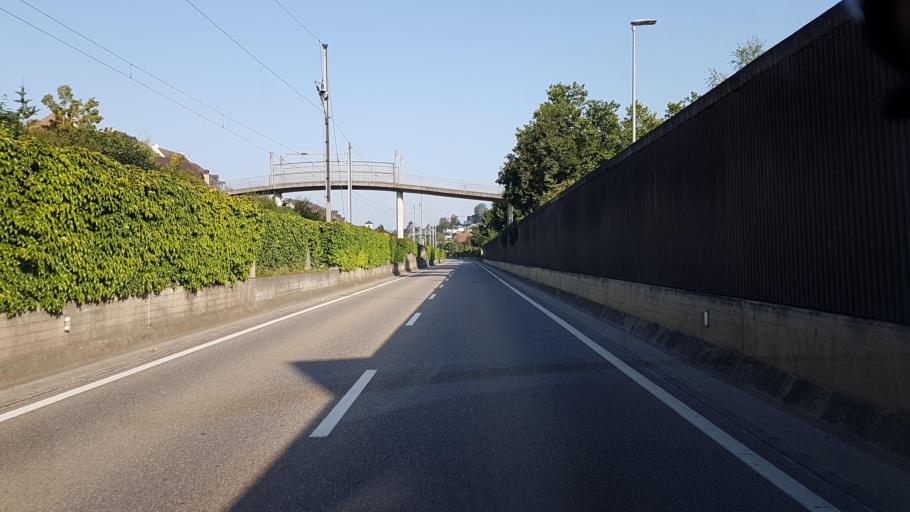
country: CH
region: Aargau
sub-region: Bezirk Zurzach
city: Klingnau
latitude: 47.5797
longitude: 8.2534
